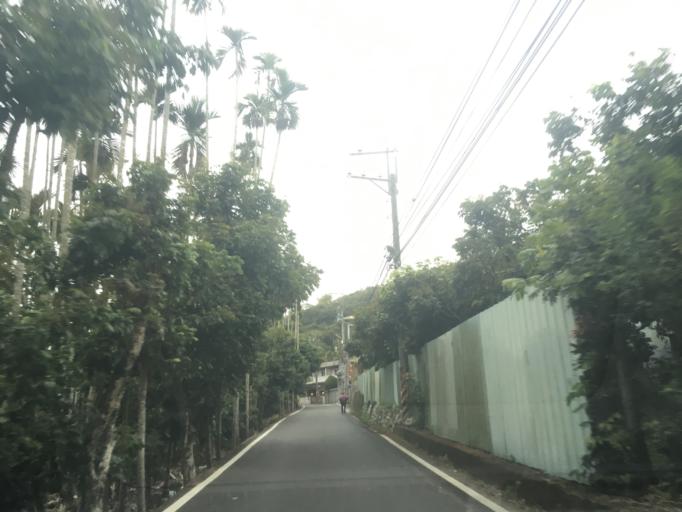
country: TW
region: Taiwan
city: Zhongxing New Village
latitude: 24.0387
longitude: 120.7195
